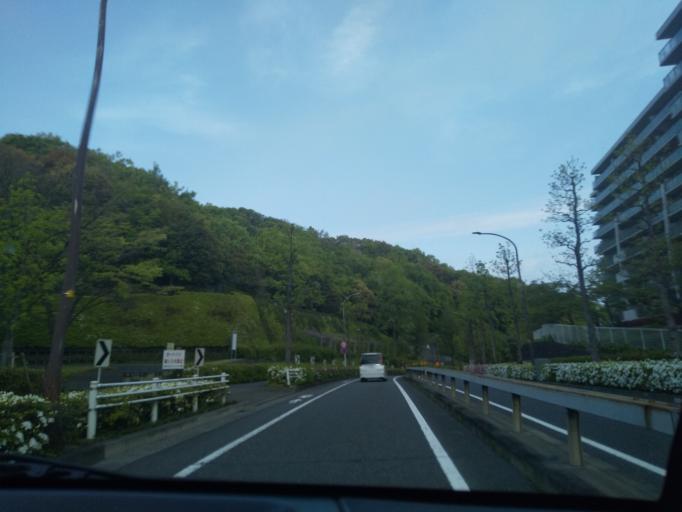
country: JP
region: Tokyo
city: Kokubunji
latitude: 35.6425
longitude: 139.4894
